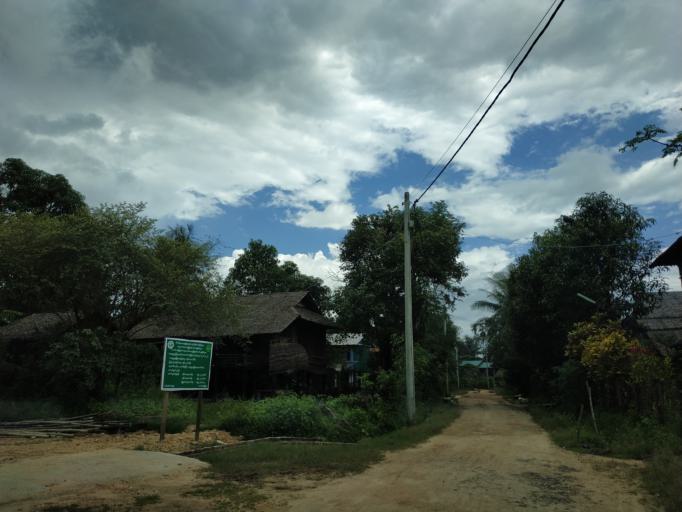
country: MM
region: Tanintharyi
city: Dawei
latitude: 14.1879
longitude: 98.1653
